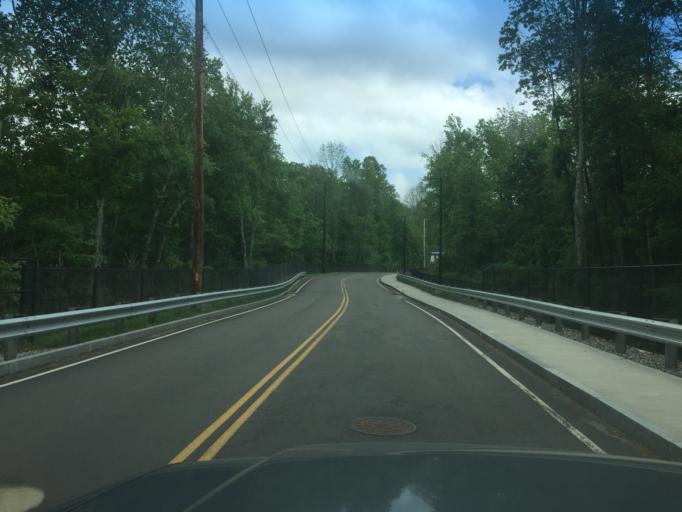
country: US
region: Massachusetts
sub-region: Worcester County
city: Milford
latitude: 42.1716
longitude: -71.5111
